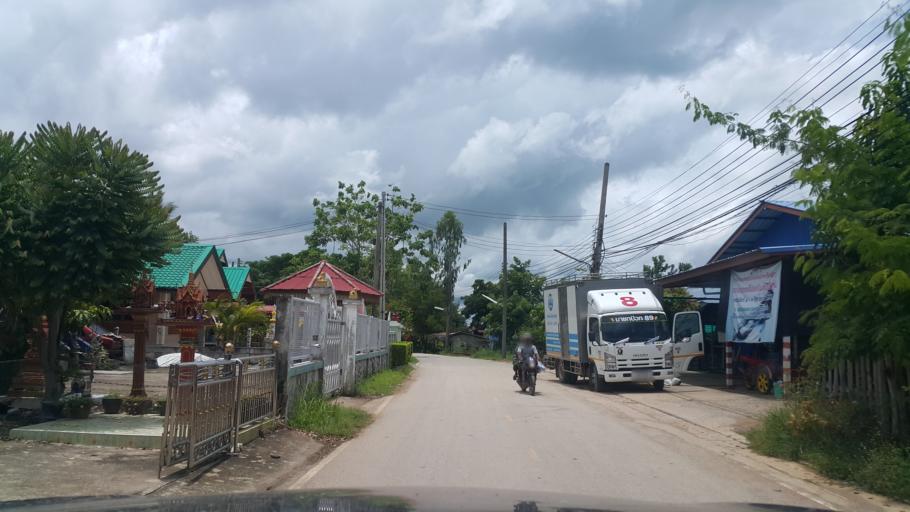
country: TH
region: Sukhothai
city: Kong Krailat
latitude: 16.9301
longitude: 99.9589
